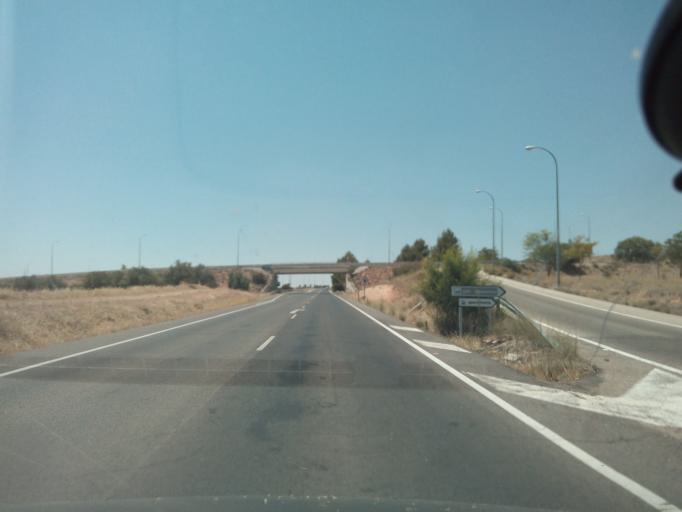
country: ES
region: Castille-La Mancha
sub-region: Province of Toledo
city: Villacanas
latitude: 39.6102
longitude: -3.3544
